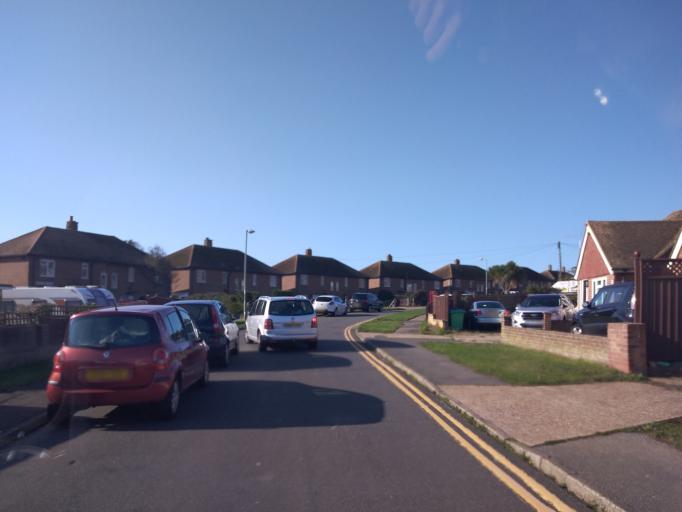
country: GB
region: England
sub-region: East Sussex
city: Newhaven
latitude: 50.7898
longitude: 0.0444
